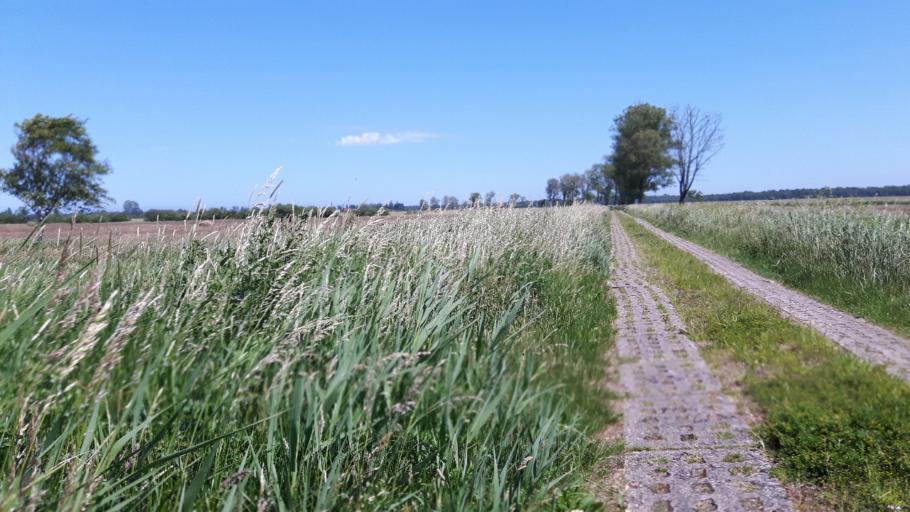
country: PL
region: Pomeranian Voivodeship
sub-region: Powiat slupski
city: Smoldzino
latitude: 54.6767
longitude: 17.2640
